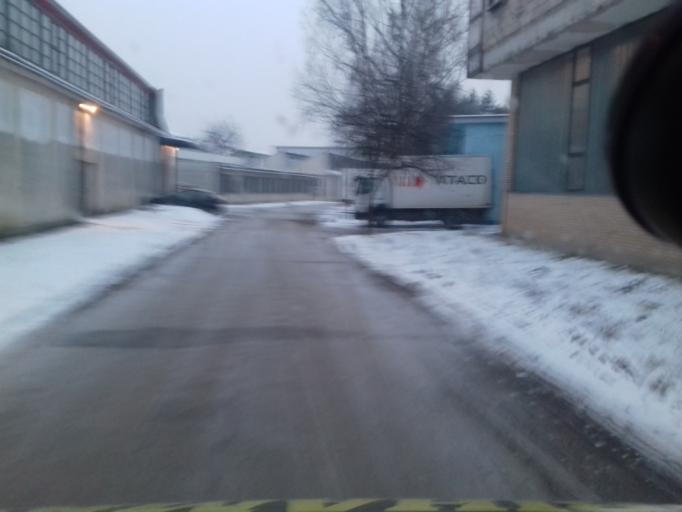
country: BA
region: Federation of Bosnia and Herzegovina
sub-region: Kanton Sarajevo
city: Sarajevo
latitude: 43.8614
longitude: 18.3704
